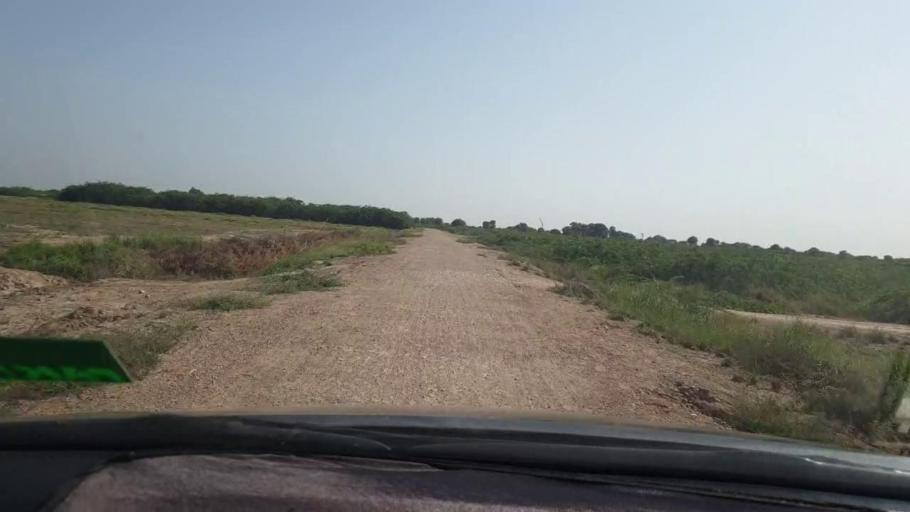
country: PK
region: Sindh
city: Naukot
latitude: 24.9283
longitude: 69.2398
